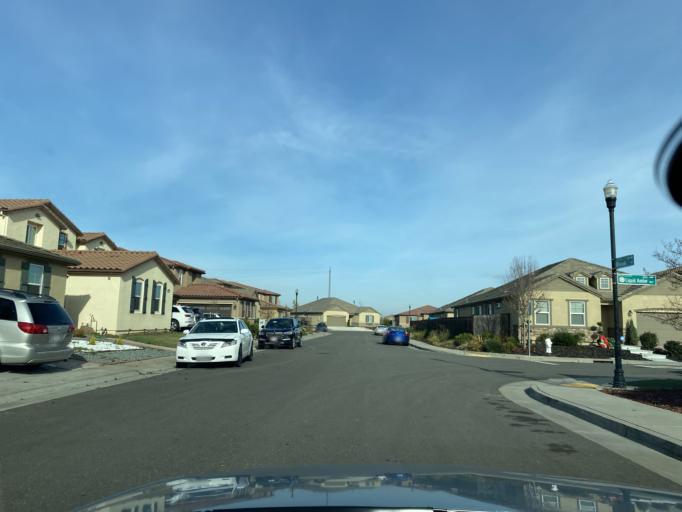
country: US
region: California
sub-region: Sacramento County
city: Elk Grove
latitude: 38.3930
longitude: -121.3942
